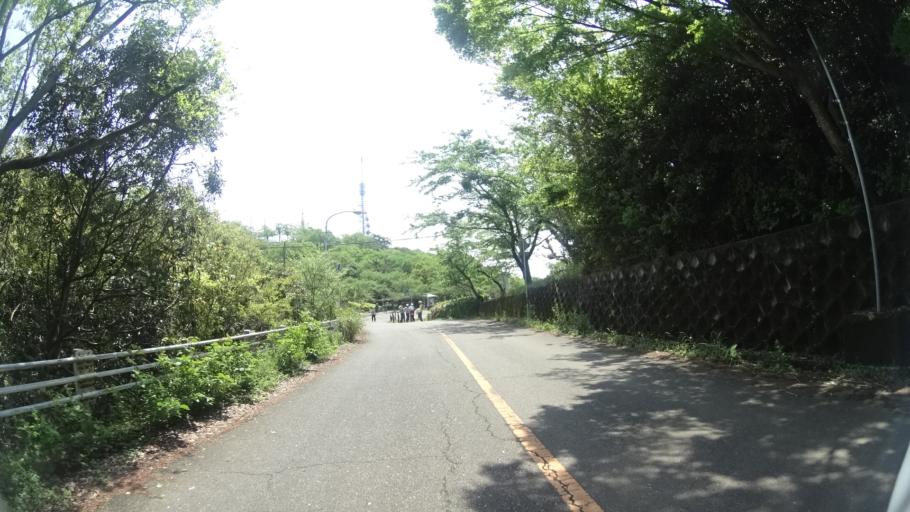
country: JP
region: Tokushima
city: Tokushima-shi
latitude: 34.0682
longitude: 134.5358
